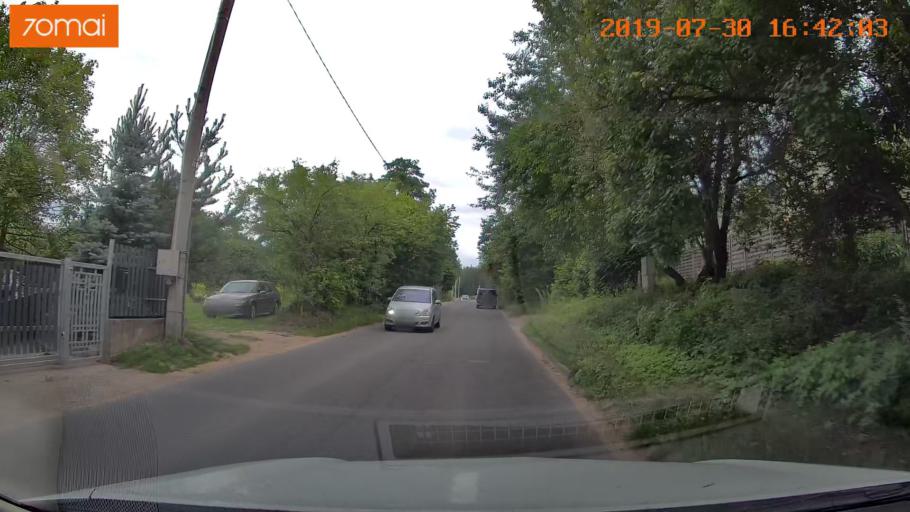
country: LT
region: Vilnius County
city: Rasos
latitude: 54.7146
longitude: 25.3515
